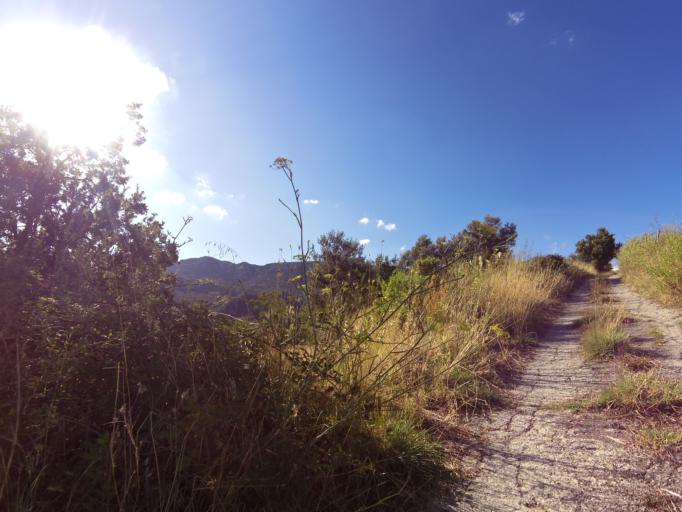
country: IT
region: Calabria
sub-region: Provincia di Reggio Calabria
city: Pazzano
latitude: 38.4448
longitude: 16.4493
